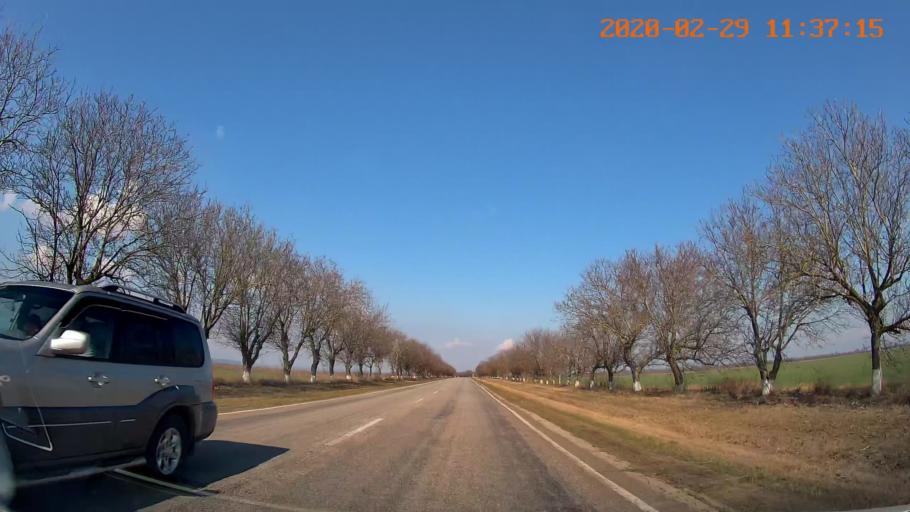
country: MD
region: Rezina
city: Saharna
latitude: 47.6090
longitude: 29.0477
